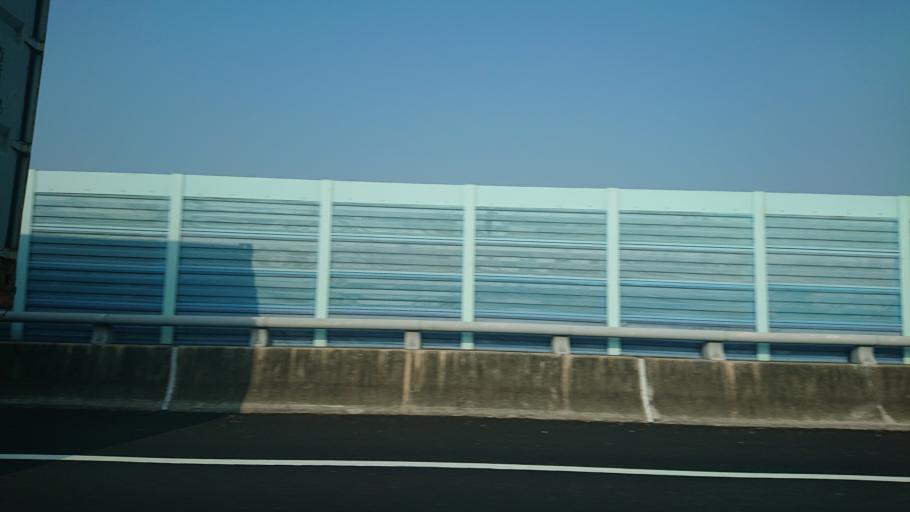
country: TW
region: Taiwan
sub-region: Changhua
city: Chang-hua
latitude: 24.1776
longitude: 120.5479
